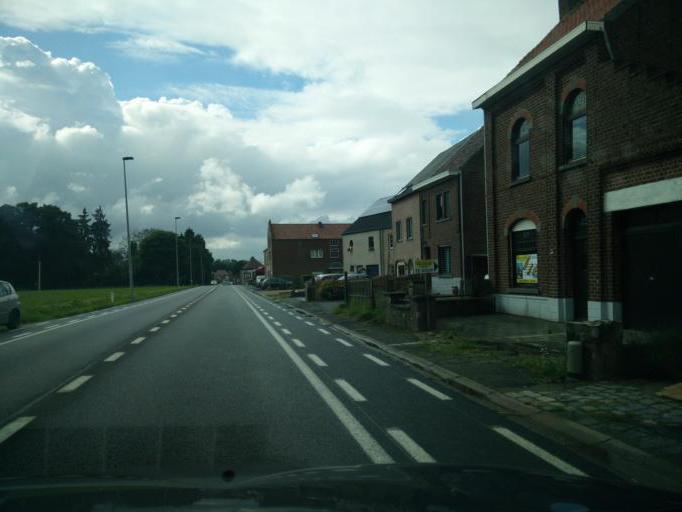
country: BE
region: Flanders
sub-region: Provincie Oost-Vlaanderen
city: Ninove
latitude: 50.7988
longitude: 4.0649
